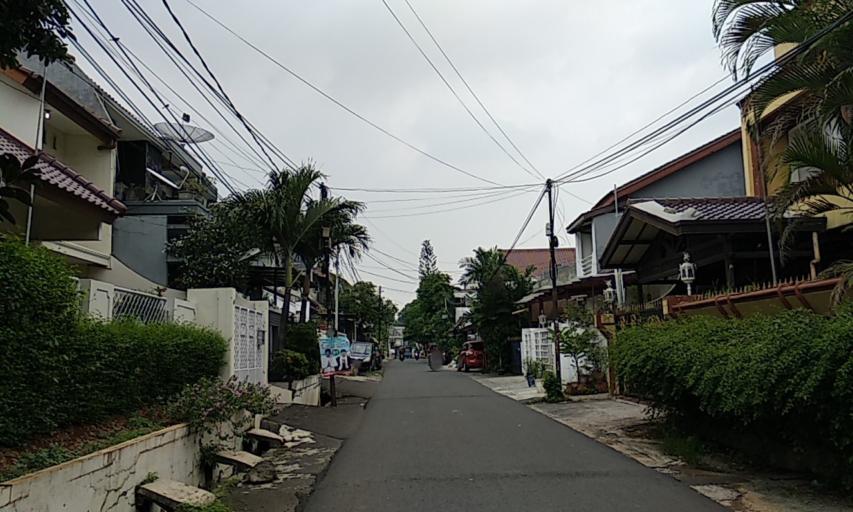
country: ID
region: Jakarta Raya
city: Jakarta
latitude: -6.2379
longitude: 106.8562
